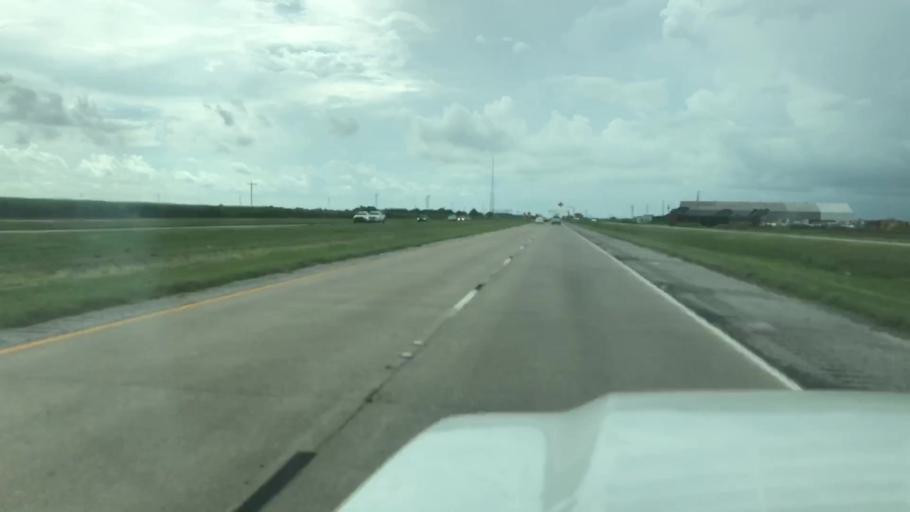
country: US
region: Louisiana
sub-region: Iberia Parish
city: Jeanerette
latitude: 29.9097
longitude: -91.7133
